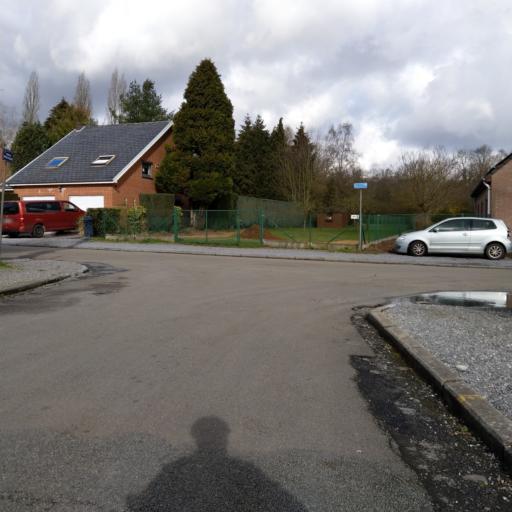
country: BE
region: Wallonia
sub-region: Province du Hainaut
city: Mons
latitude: 50.4833
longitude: 3.9406
